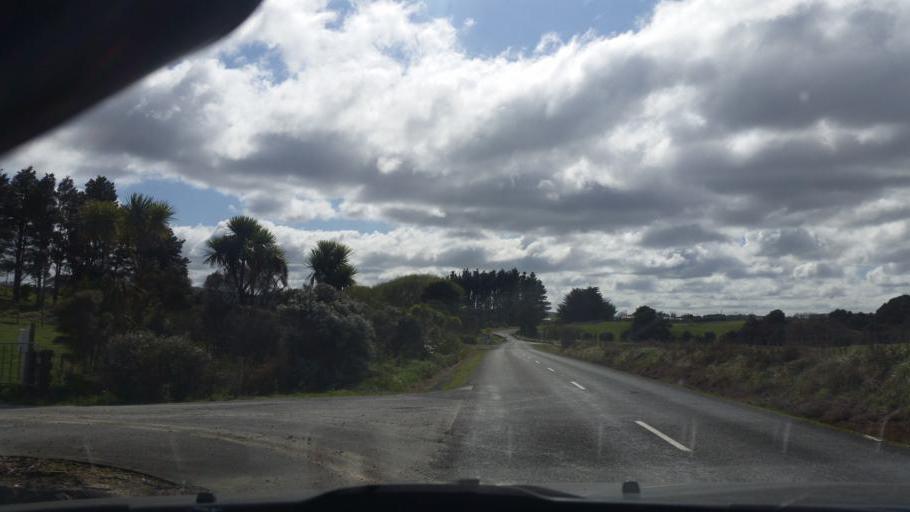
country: NZ
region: Auckland
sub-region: Auckland
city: Wellsford
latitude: -36.1498
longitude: 174.5030
